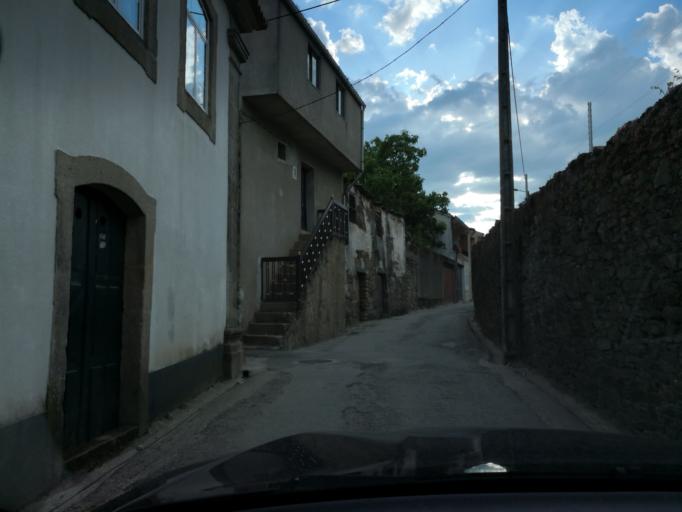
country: PT
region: Vila Real
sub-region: Sabrosa
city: Vilela
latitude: 41.2081
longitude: -7.6610
